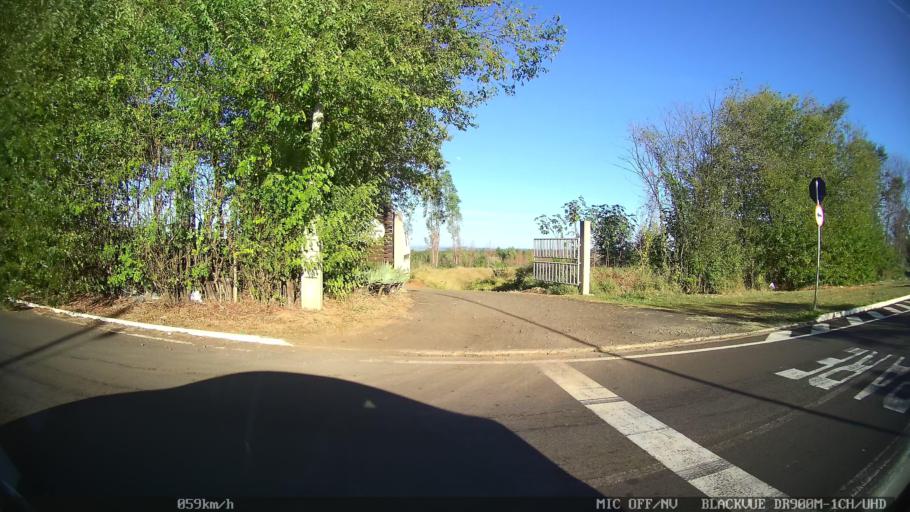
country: BR
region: Sao Paulo
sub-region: Franca
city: Franca
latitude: -20.5801
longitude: -47.3854
